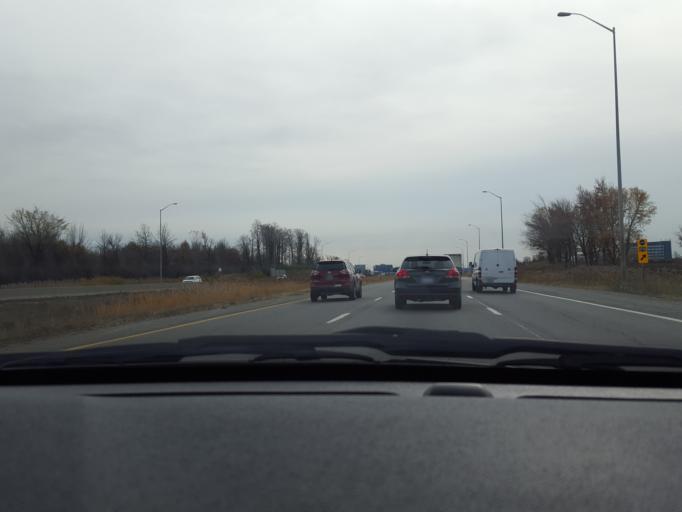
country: CA
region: Ontario
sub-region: York
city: Richmond Hill
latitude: 43.8738
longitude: -79.3778
